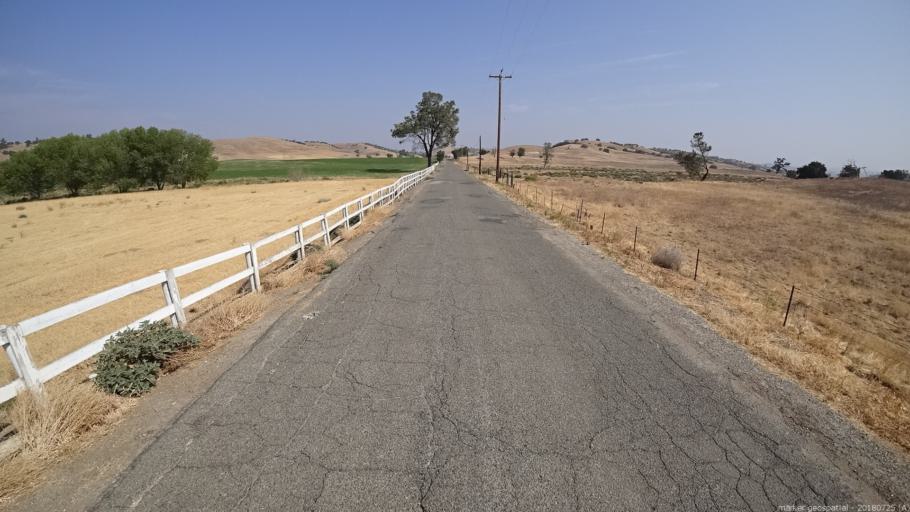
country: US
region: California
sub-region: San Luis Obispo County
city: San Miguel
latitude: 35.8217
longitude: -120.6554
